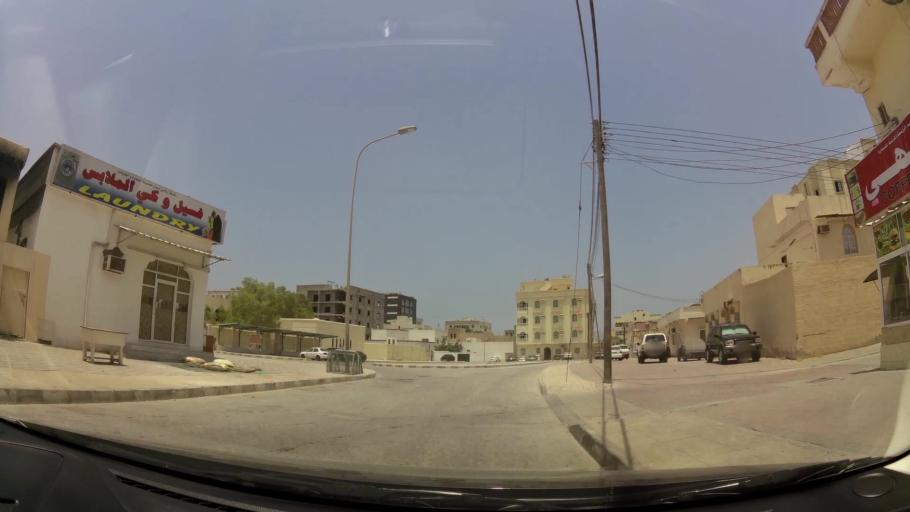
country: OM
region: Zufar
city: Salalah
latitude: 17.0179
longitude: 54.1082
